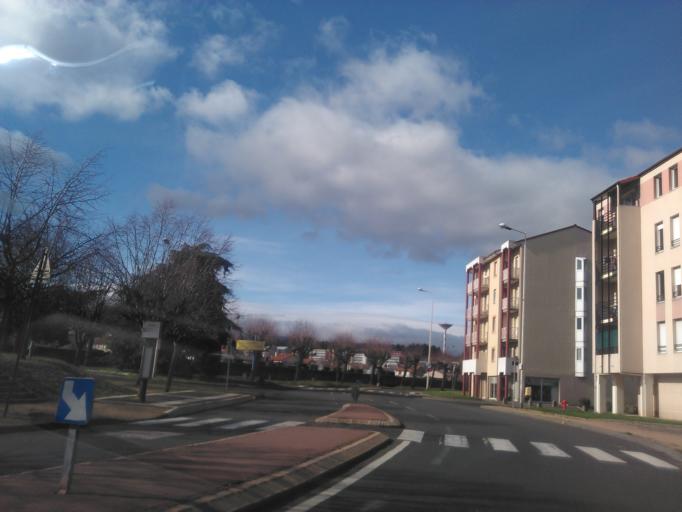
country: FR
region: Auvergne
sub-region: Departement du Puy-de-Dome
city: Aubiere
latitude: 45.7530
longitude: 3.1177
